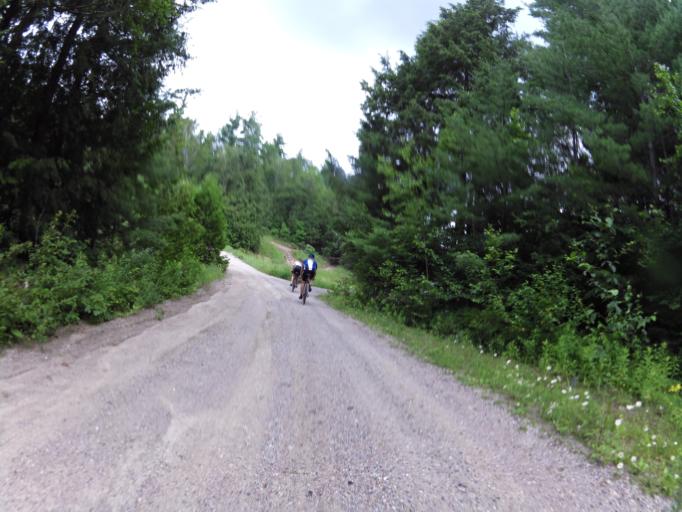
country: CA
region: Ontario
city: Perth
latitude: 45.0169
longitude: -76.5986
